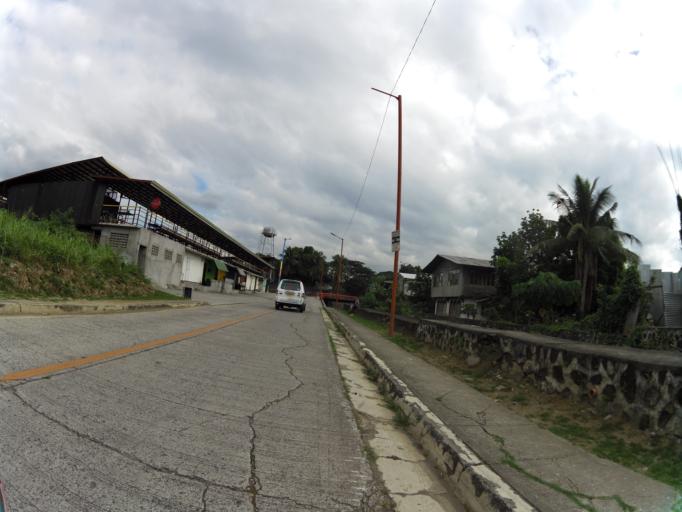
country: PH
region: Calabarzon
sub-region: Province of Rizal
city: Antipolo
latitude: 14.6420
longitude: 121.1050
